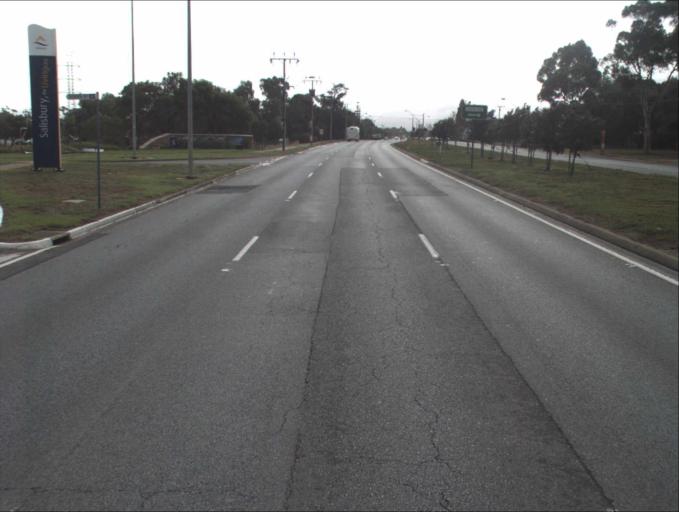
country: AU
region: South Australia
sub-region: Port Adelaide Enfield
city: Enfield
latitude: -34.8342
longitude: 138.6102
